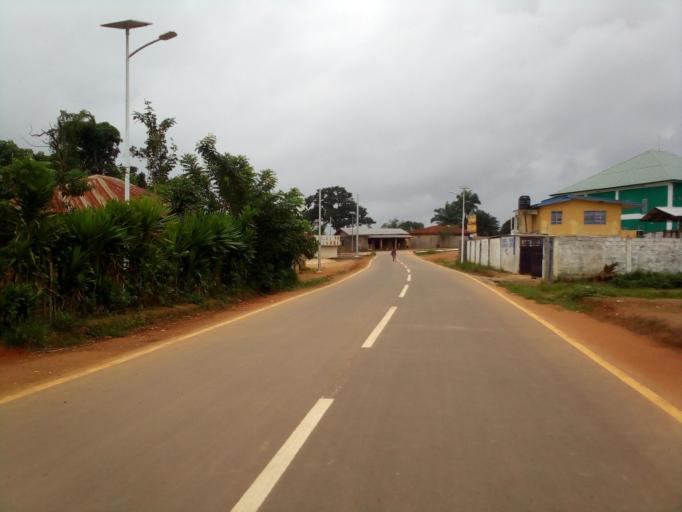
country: SL
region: Eastern Province
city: Kailahun
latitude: 8.2748
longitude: -10.5796
